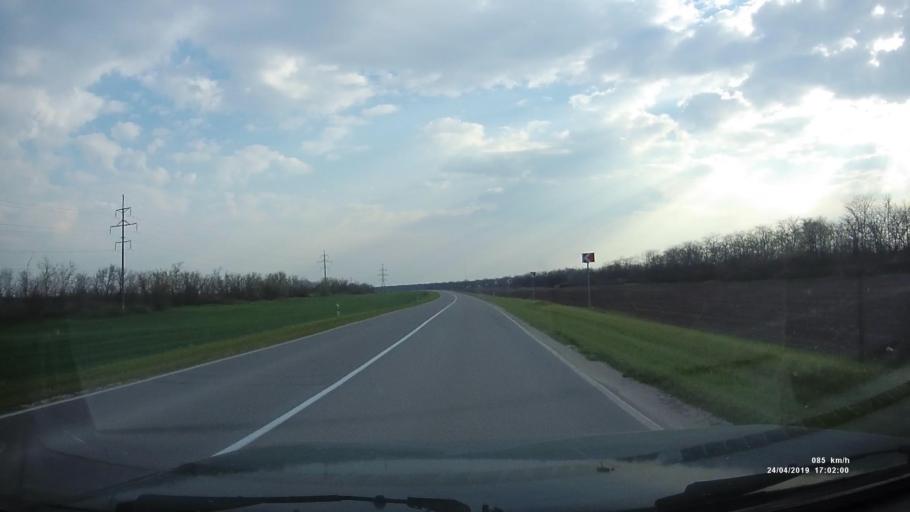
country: RU
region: Rostov
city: Sal'sk
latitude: 46.5858
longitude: 41.6187
